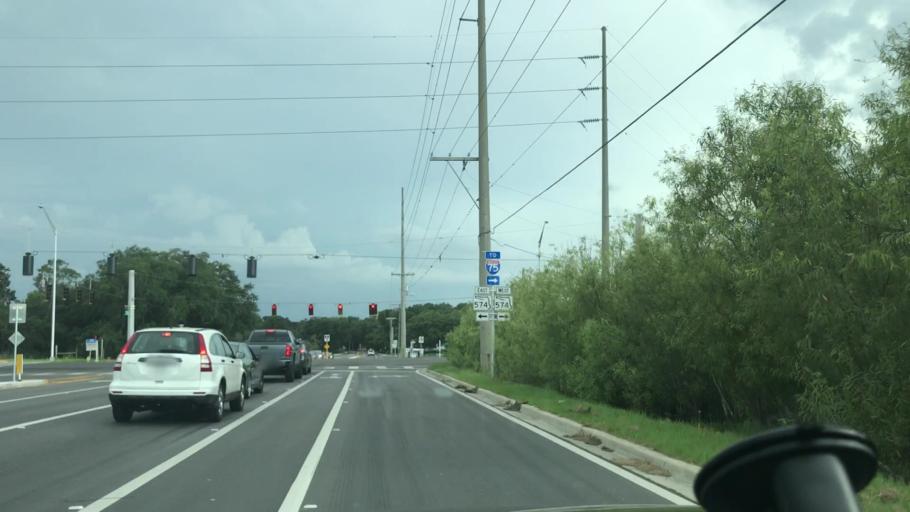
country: US
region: Florida
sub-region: Hillsborough County
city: Mango
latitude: 27.9821
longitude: -82.3188
